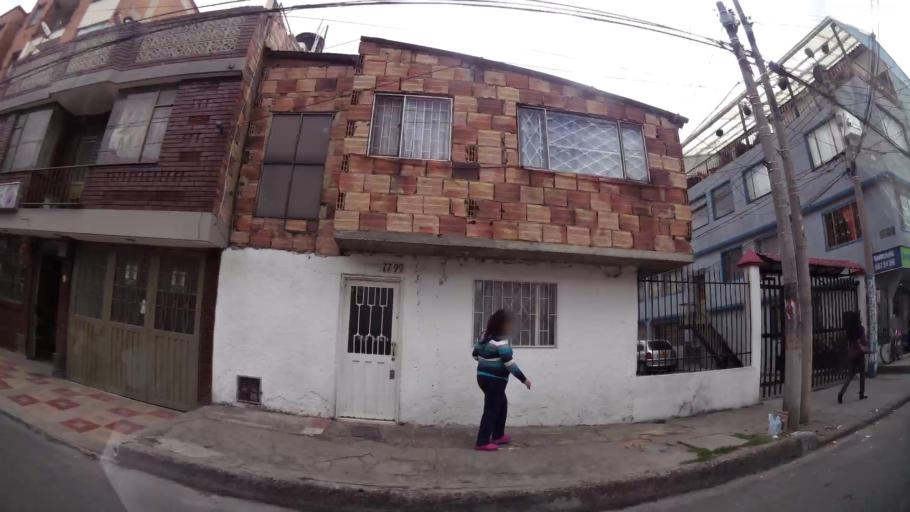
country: CO
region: Bogota D.C.
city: Barrio San Luis
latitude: 4.7035
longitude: -74.0908
